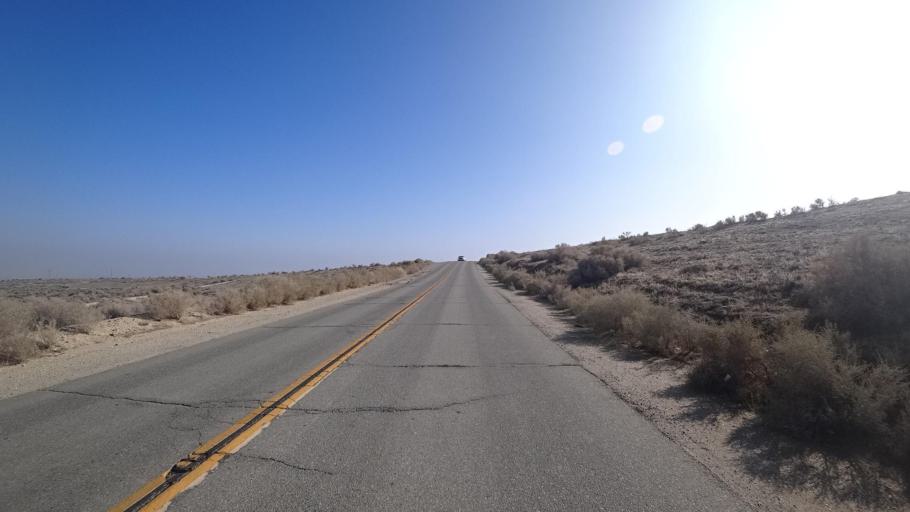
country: US
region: California
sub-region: Kern County
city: Taft Heights
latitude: 35.1409
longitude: -119.4978
